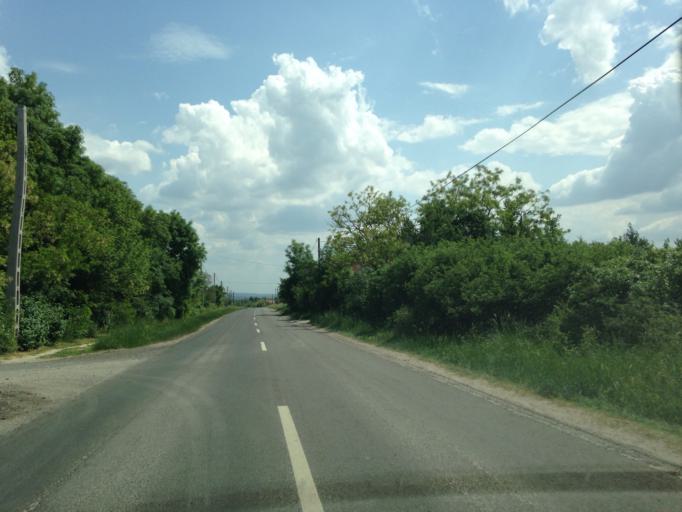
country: HU
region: Pest
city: Szentendre
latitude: 47.6876
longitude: 19.0554
